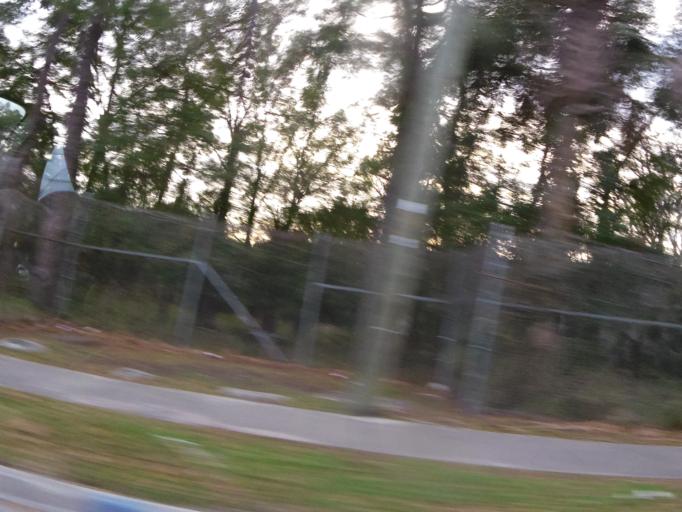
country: US
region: Florida
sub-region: Duval County
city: Jacksonville
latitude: 30.3635
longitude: -81.7057
